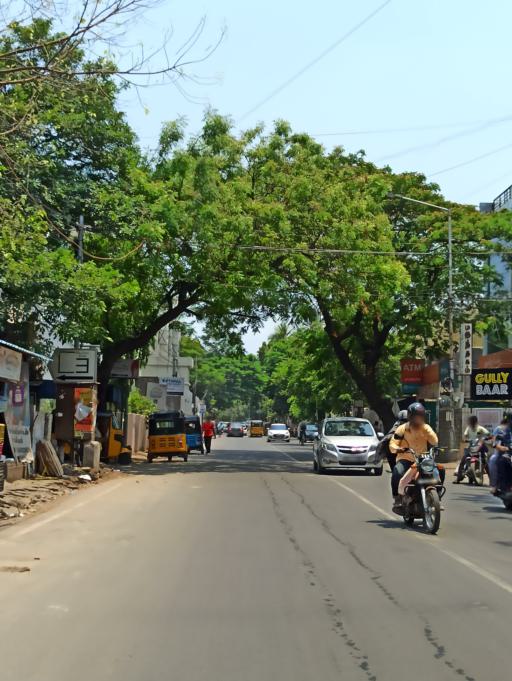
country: IN
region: Tamil Nadu
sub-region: Chennai
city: Chetput
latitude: 13.0789
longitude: 80.2336
